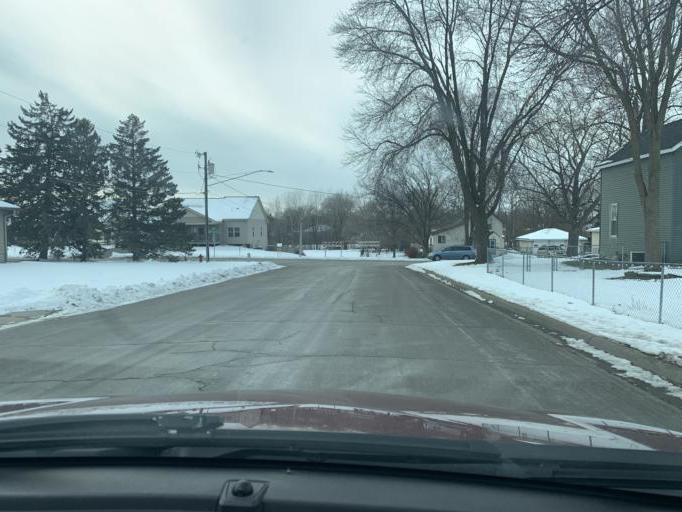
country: US
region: Minnesota
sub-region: Washington County
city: Saint Paul Park
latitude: 44.8460
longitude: -92.9922
